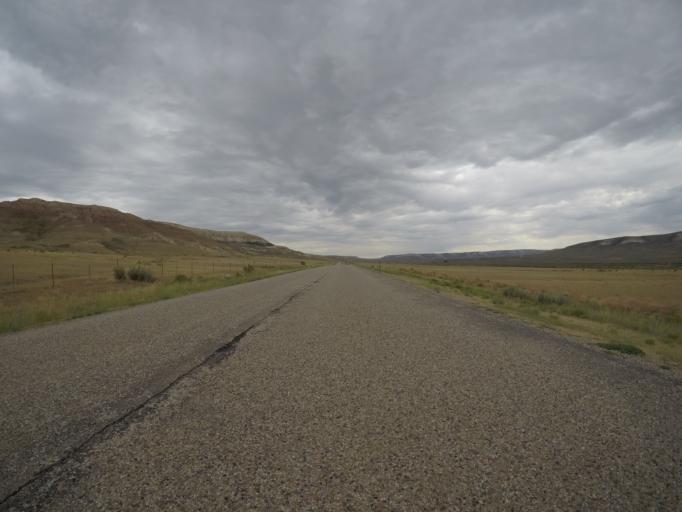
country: US
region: Wyoming
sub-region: Lincoln County
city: Kemmerer
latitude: 41.8230
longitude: -110.7480
